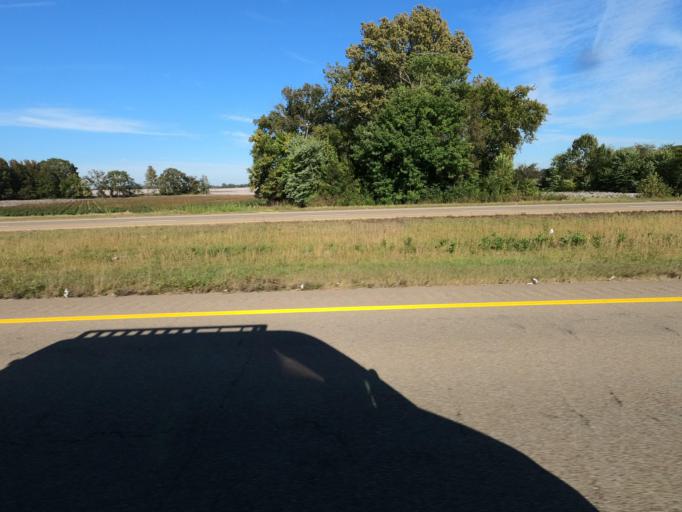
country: US
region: Tennessee
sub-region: Crockett County
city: Alamo
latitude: 35.8552
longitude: -89.2002
